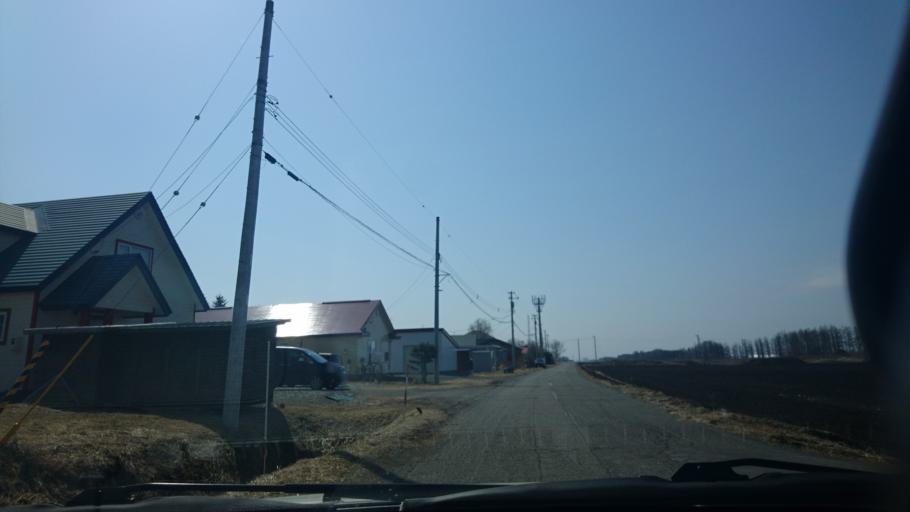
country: JP
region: Hokkaido
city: Otofuke
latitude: 43.0948
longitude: 143.2257
